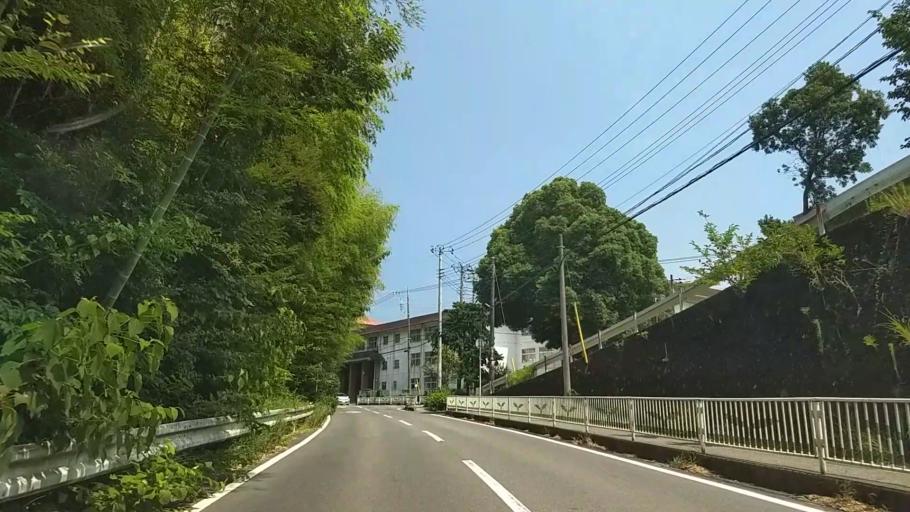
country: JP
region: Shizuoka
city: Ito
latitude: 34.9337
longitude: 139.1046
